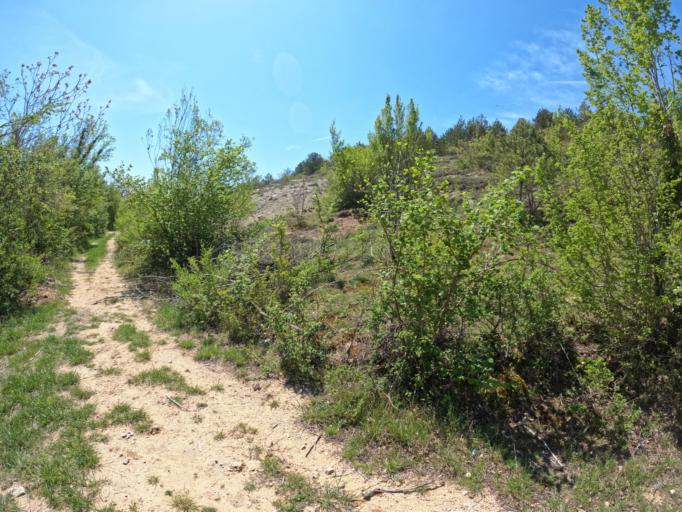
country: HR
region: Splitsko-Dalmatinska
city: Gala
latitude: 43.7222
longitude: 16.7014
